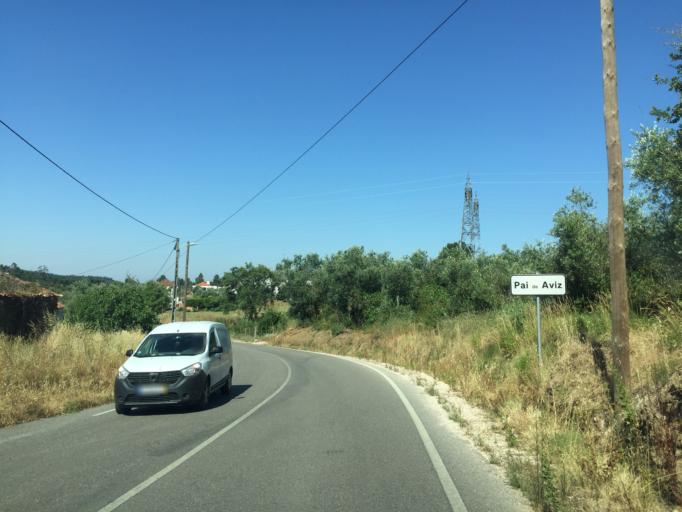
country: PT
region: Santarem
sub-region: Tomar
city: Tomar
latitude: 39.5977
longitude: -8.3184
